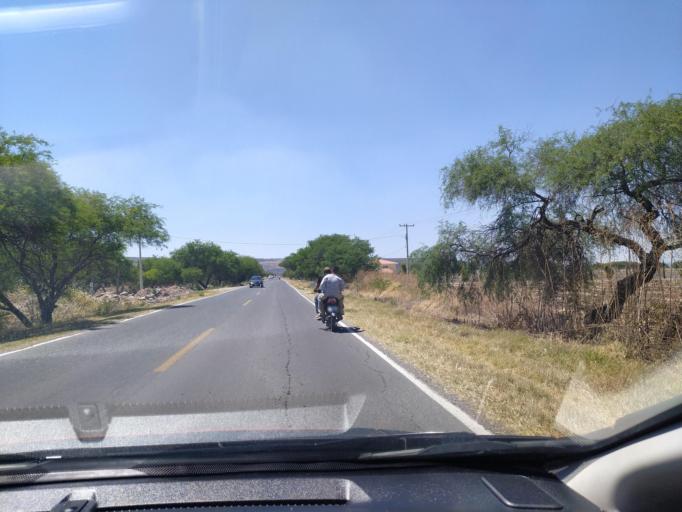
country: MX
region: Guanajuato
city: Ciudad Manuel Doblado
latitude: 20.7412
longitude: -101.9352
